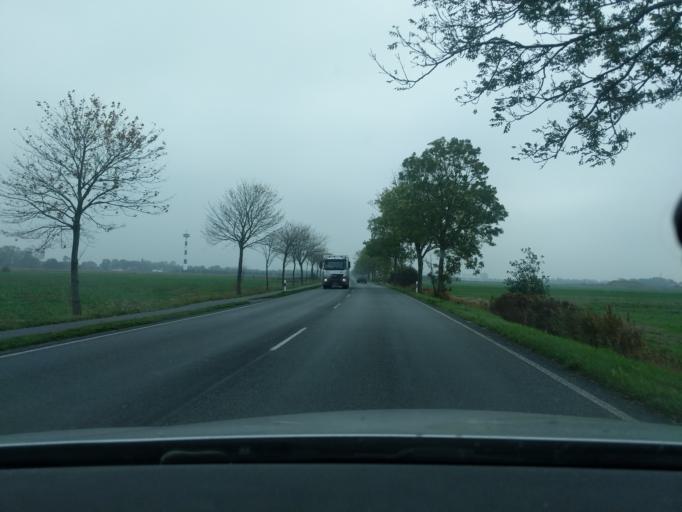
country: DE
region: Lower Saxony
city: Cuxhaven
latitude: 53.8309
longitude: 8.7457
